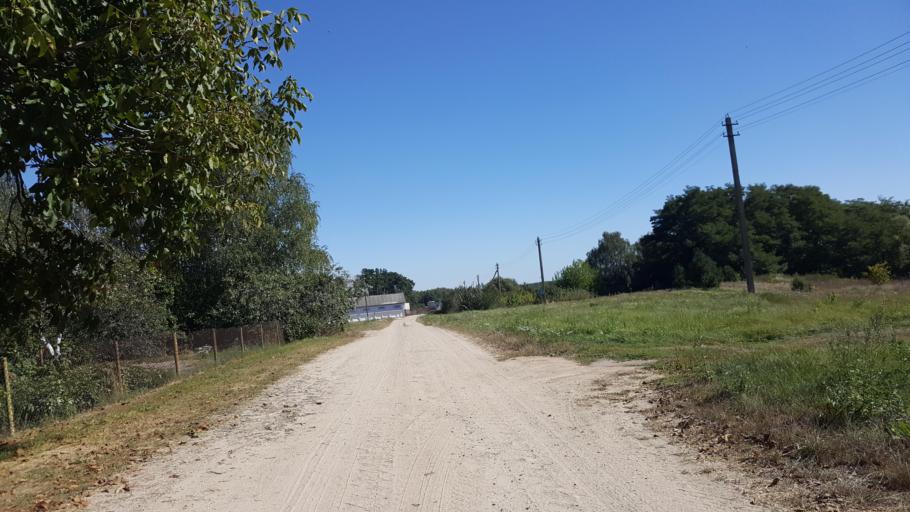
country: PL
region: Lublin Voivodeship
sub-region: Powiat bialski
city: Rokitno
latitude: 52.2126
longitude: 23.3965
